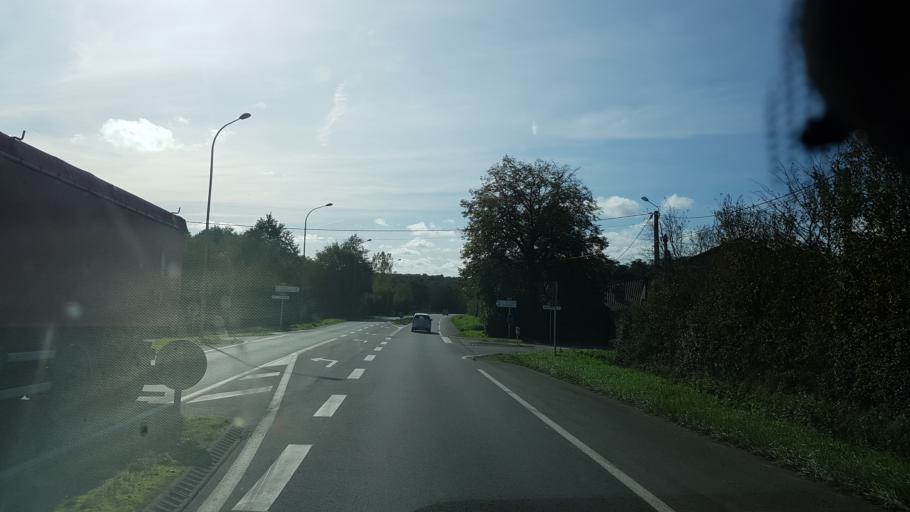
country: FR
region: Poitou-Charentes
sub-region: Departement de la Charente
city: Loubert
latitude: 45.9449
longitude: 0.5512
